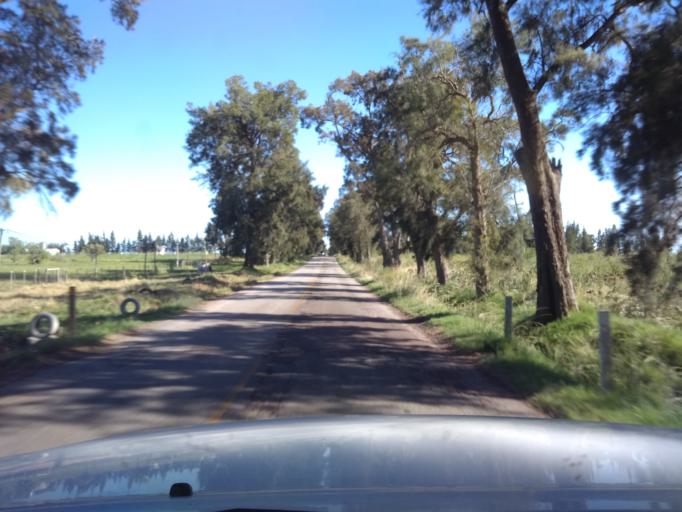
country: UY
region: Canelones
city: San Bautista
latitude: -34.3694
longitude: -55.9595
